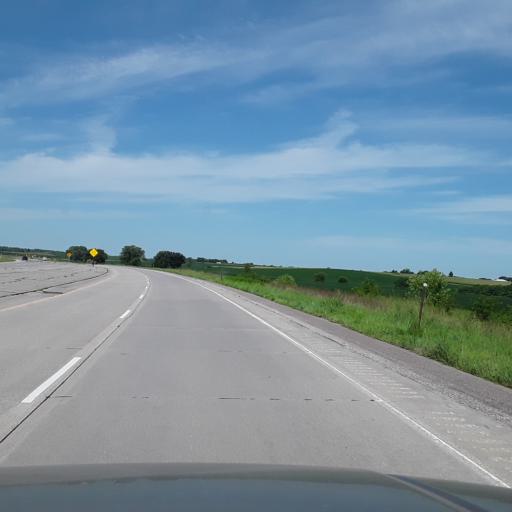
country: US
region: Nebraska
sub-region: Lancaster County
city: Lincoln
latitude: 40.8882
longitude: -96.8001
